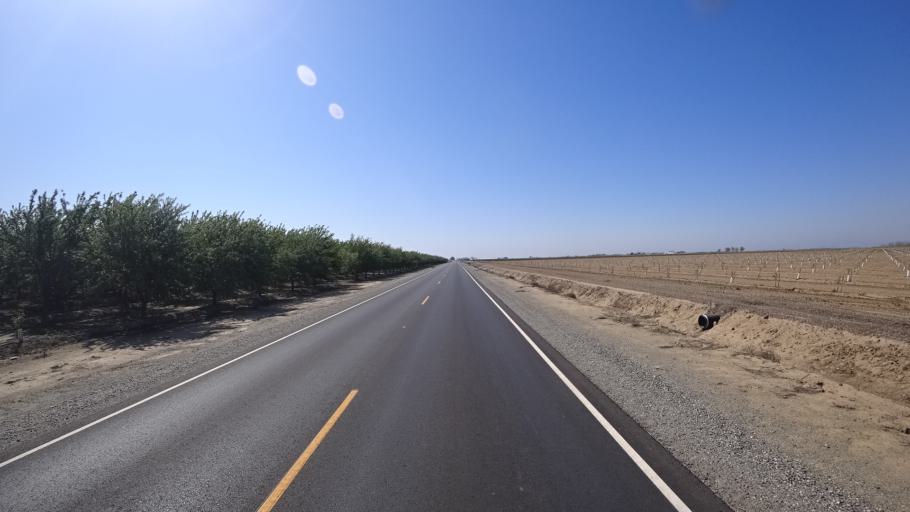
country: US
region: California
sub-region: Glenn County
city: Hamilton City
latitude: 39.6332
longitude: -122.0650
